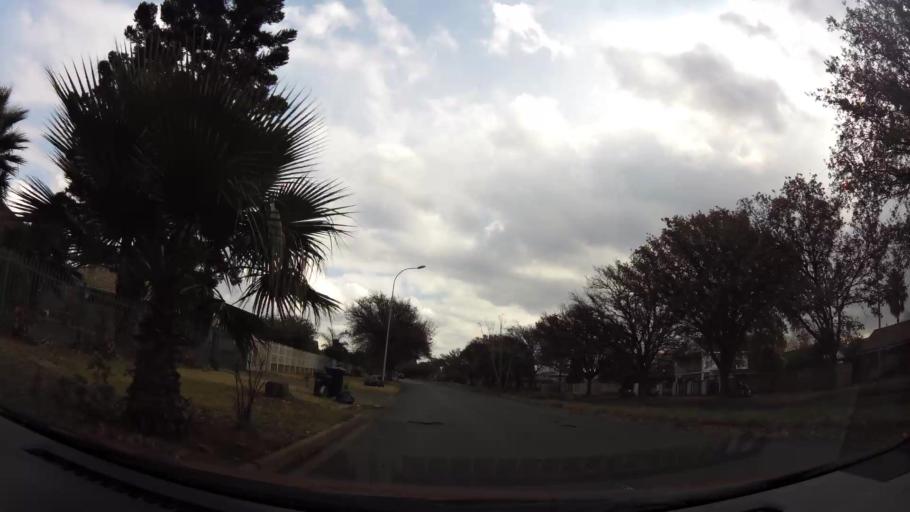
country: ZA
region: Gauteng
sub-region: Sedibeng District Municipality
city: Vanderbijlpark
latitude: -26.7174
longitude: 27.8553
